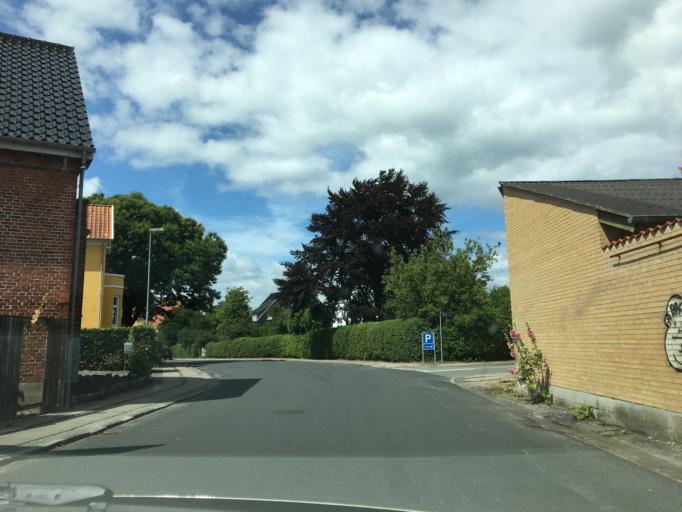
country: DK
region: South Denmark
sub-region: Langeland Kommune
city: Rudkobing
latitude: 54.9387
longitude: 10.7159
